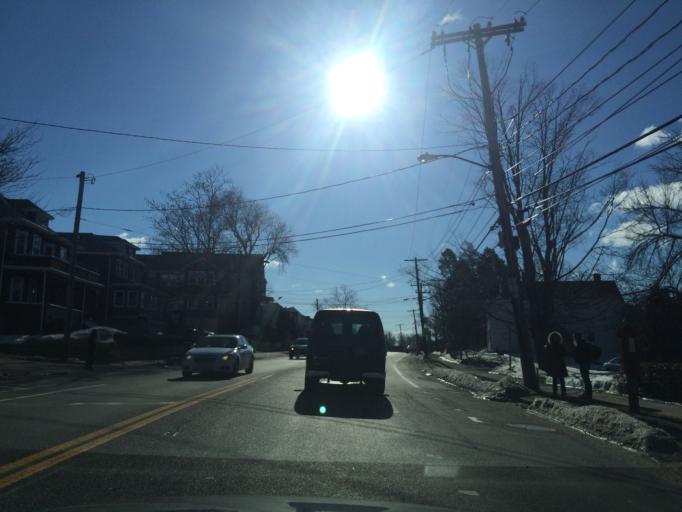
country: US
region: Massachusetts
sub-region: Middlesex County
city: Watertown
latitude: 42.3729
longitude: -71.2016
